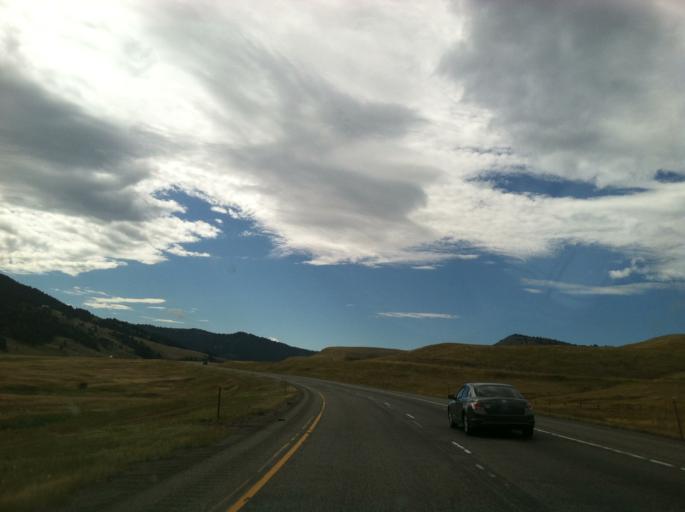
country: US
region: Montana
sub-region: Park County
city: Livingston
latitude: 45.6637
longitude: -110.7189
